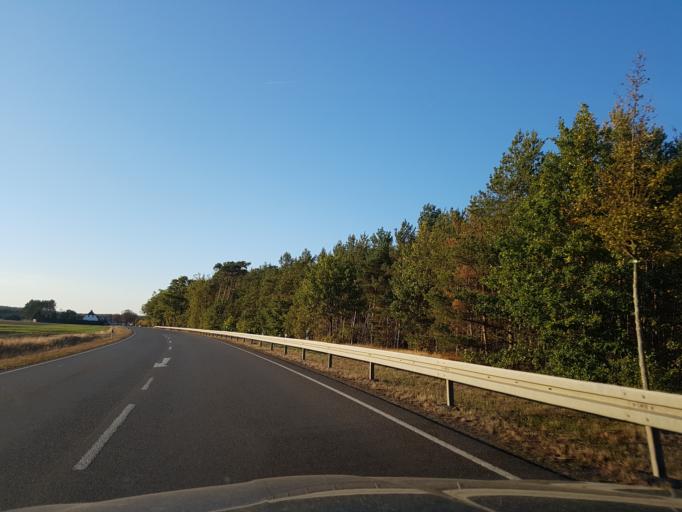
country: DE
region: Brandenburg
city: Bad Liebenwerda
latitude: 51.5432
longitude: 13.3936
